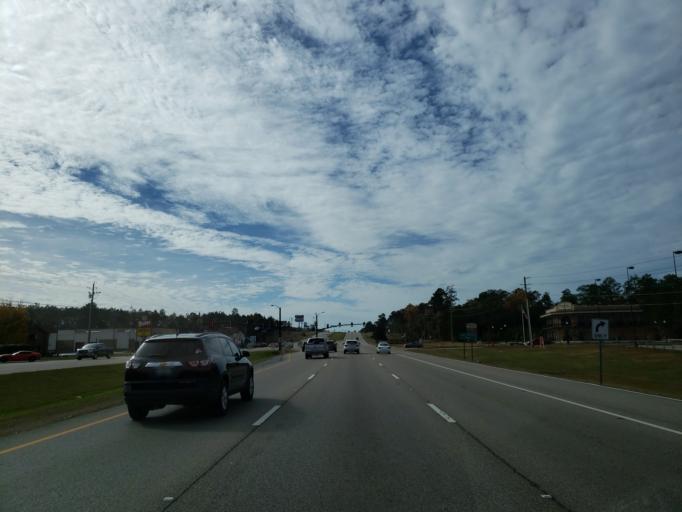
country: US
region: Mississippi
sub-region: Lamar County
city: West Hattiesburg
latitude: 31.3209
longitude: -89.3868
